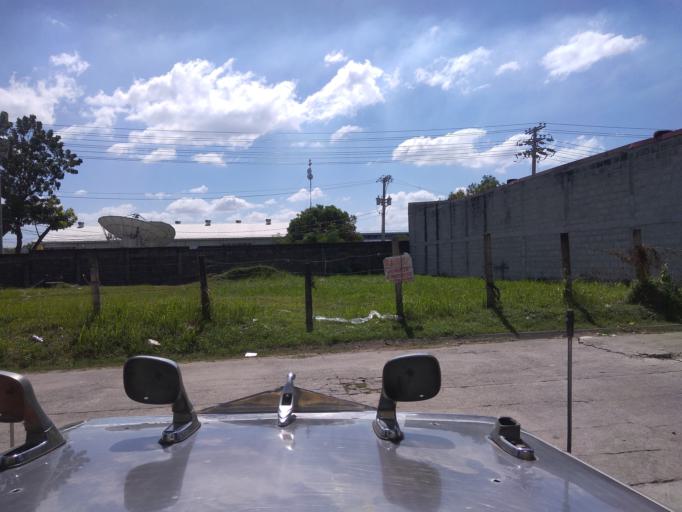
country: PH
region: Central Luzon
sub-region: Province of Pampanga
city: Calibutbut
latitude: 15.1146
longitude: 120.6007
